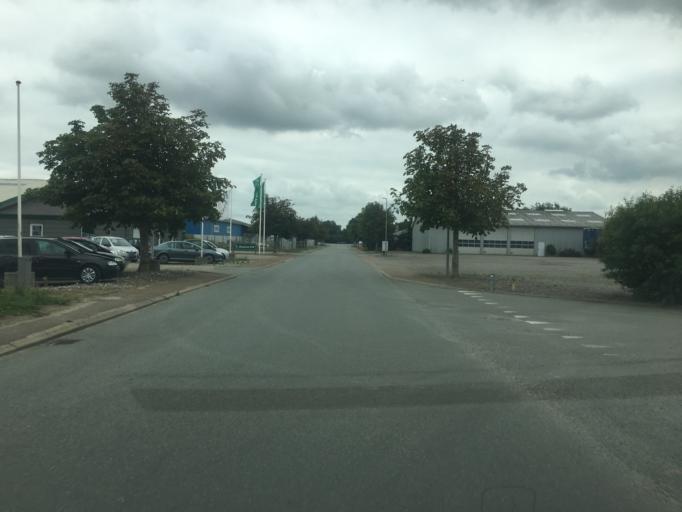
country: DK
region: South Denmark
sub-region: Tonder Kommune
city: Tonder
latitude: 54.9495
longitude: 8.8645
